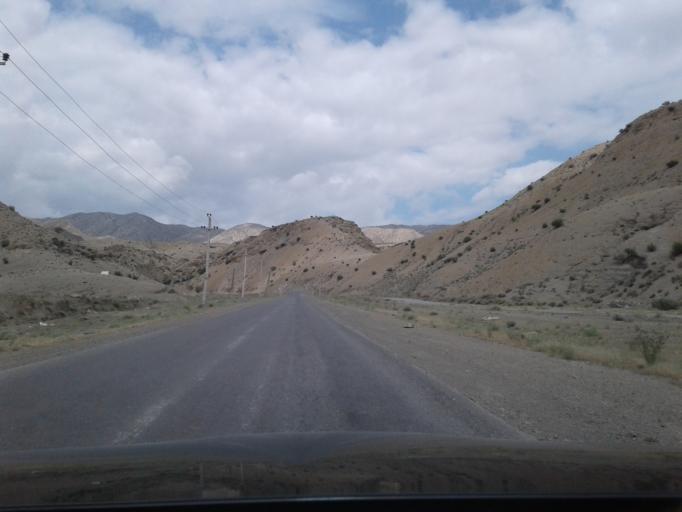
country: TM
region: Ahal
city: Baharly
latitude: 38.5018
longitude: 57.0847
